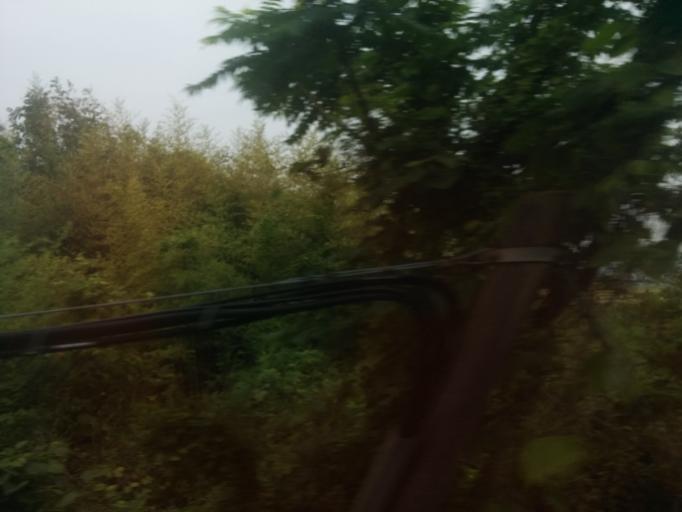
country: JP
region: Shiga Prefecture
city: Hikone
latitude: 35.2124
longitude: 136.2078
